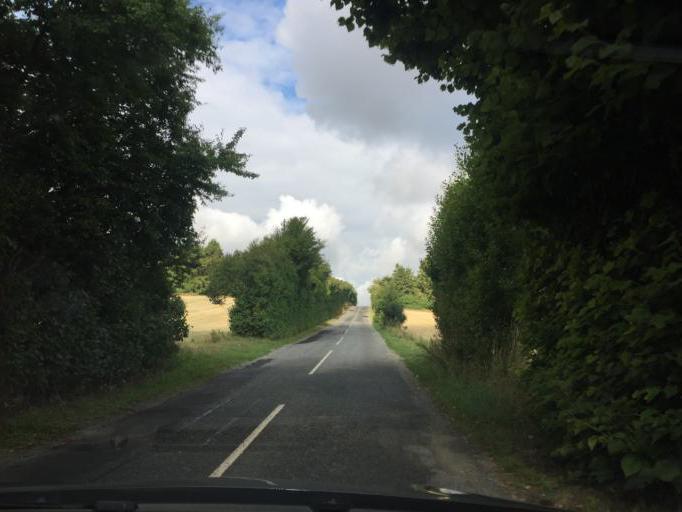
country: DK
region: South Denmark
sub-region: Assens Kommune
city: Harby
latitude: 55.1958
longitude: 10.1938
